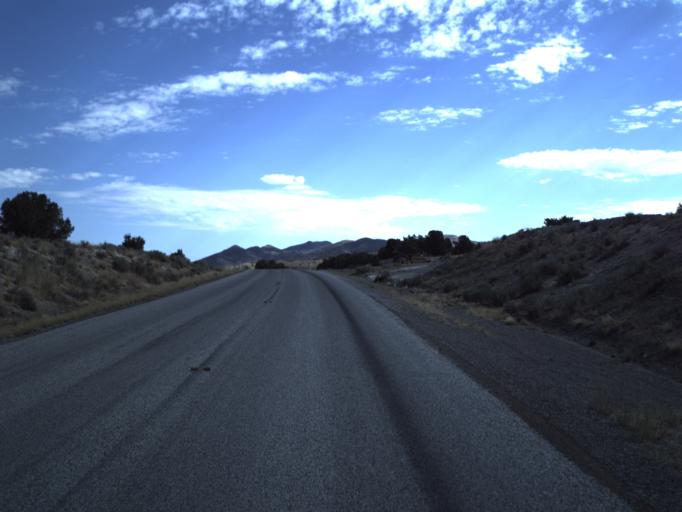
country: US
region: Utah
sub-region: Juab County
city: Mona
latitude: 39.7756
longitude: -112.1546
